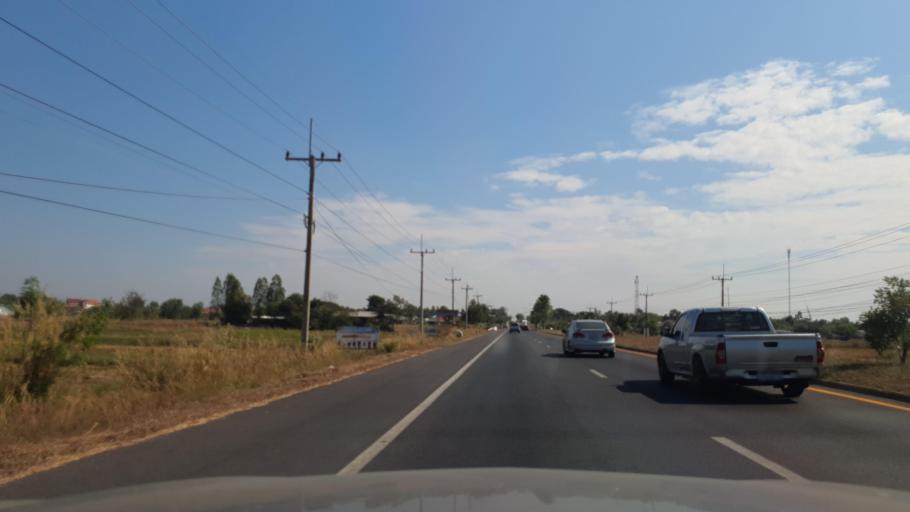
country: TH
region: Maha Sarakham
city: Chiang Yuen
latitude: 16.3777
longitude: 103.1797
